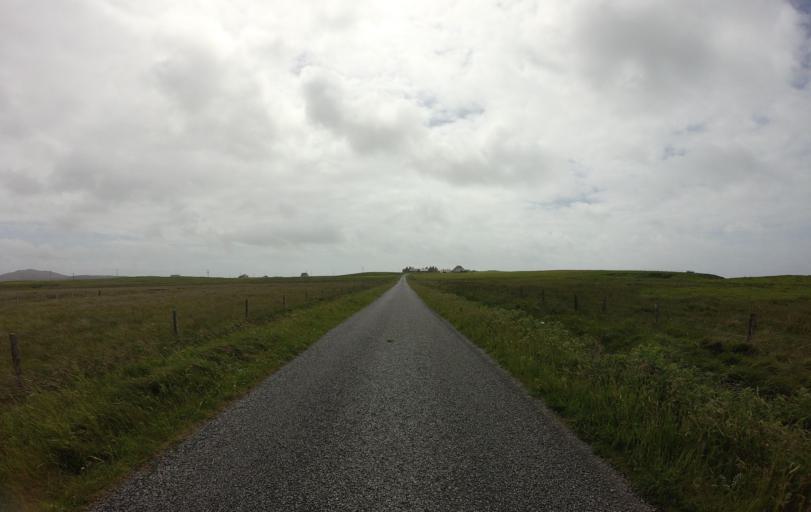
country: GB
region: Scotland
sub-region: Eilean Siar
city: Isle of South Uist
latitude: 57.2641
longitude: -7.4049
